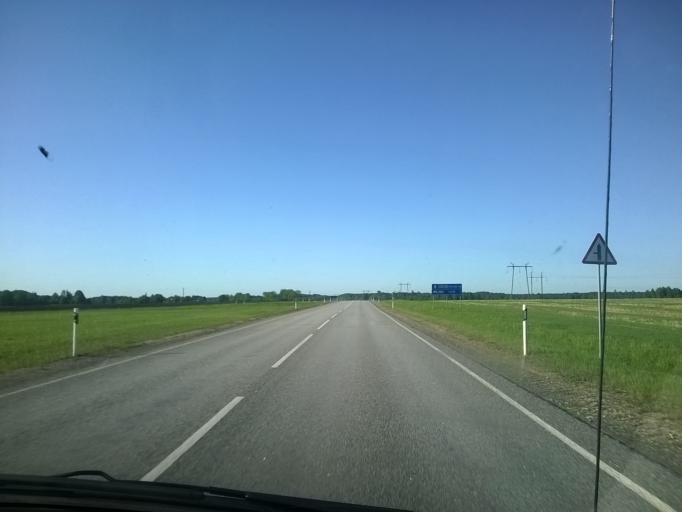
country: EE
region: Valgamaa
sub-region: Valga linn
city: Valga
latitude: 57.9439
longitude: 26.1686
